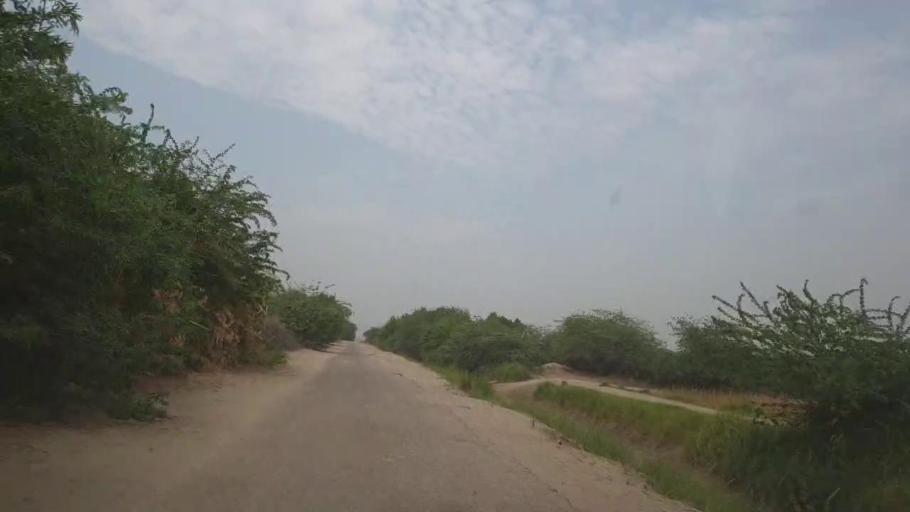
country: PK
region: Sindh
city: Kot Diji
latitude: 27.4384
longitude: 68.7131
